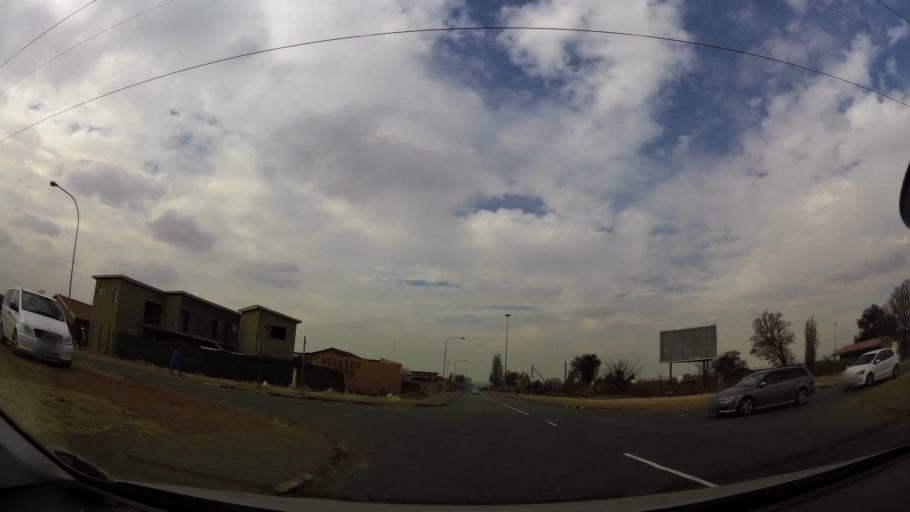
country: ZA
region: Gauteng
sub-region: City of Johannesburg Metropolitan Municipality
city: Soweto
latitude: -26.2729
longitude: 27.8606
